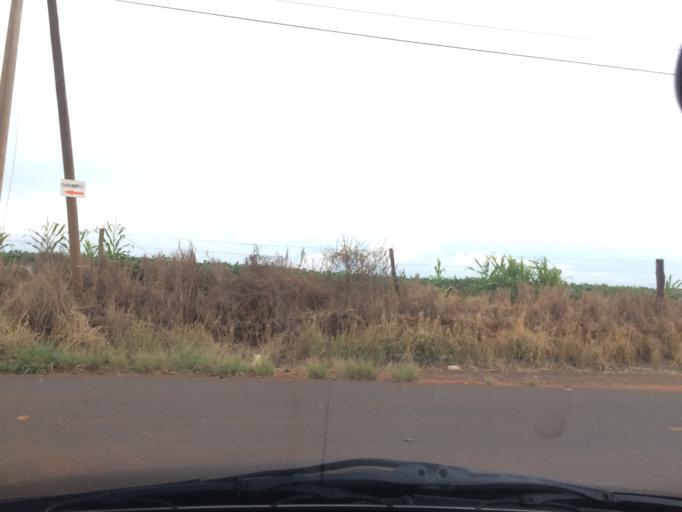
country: BR
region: Sao Paulo
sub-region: Casa Branca
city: Casa Branca
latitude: -21.7571
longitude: -47.1187
